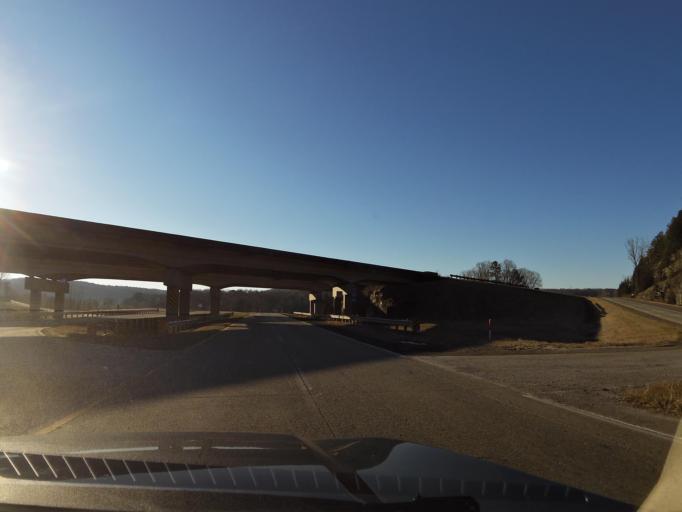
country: US
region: Alabama
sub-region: Morgan County
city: Falkville
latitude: 34.3171
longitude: -86.9011
